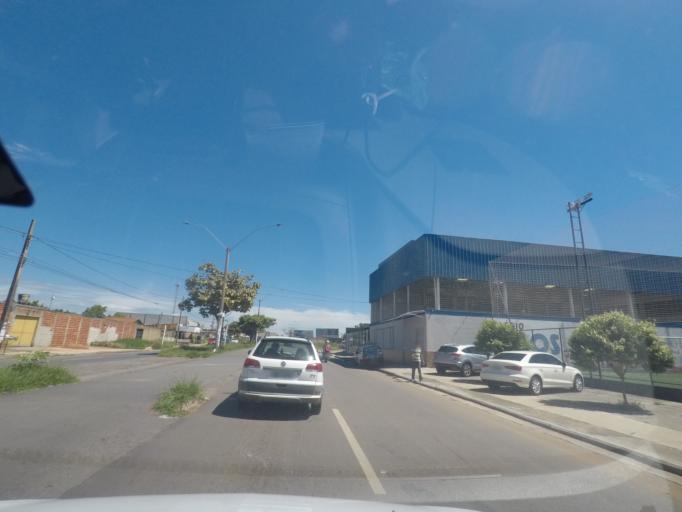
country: BR
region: Goias
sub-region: Aparecida De Goiania
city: Aparecida de Goiania
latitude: -16.7762
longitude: -49.3371
